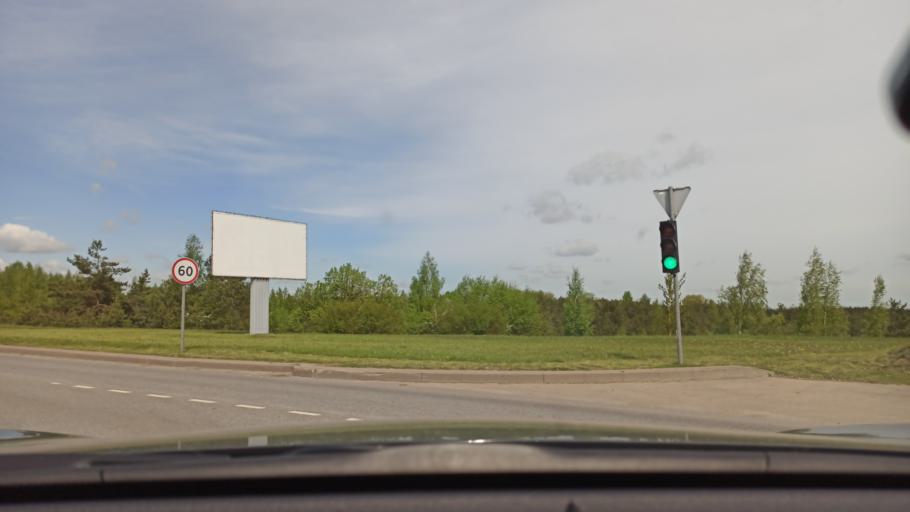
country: LT
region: Siauliu apskritis
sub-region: Siauliai
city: Siauliai
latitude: 55.9228
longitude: 23.3632
